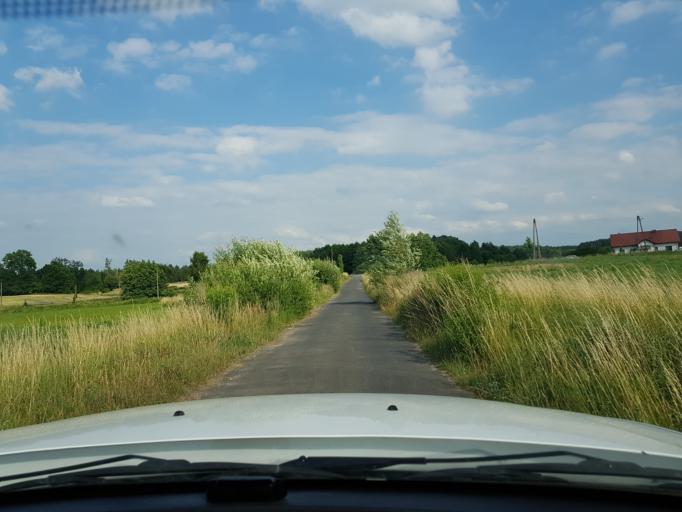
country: PL
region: West Pomeranian Voivodeship
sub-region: Powiat gryfinski
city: Chojna
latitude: 52.9959
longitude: 14.4875
